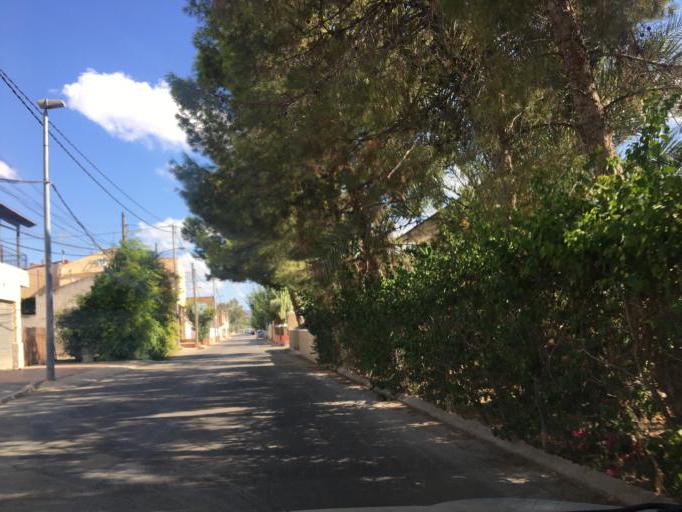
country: ES
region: Murcia
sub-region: Murcia
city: Santomera
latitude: 38.0280
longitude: -1.0478
